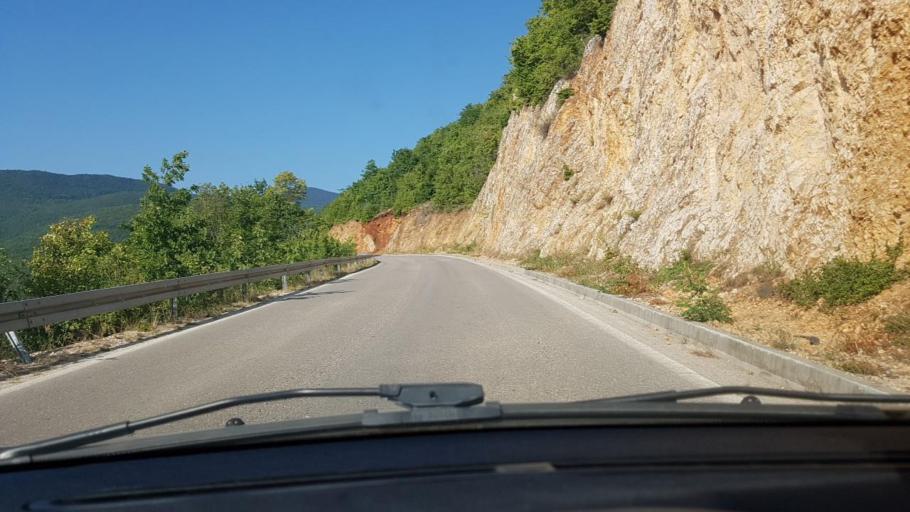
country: BA
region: Federation of Bosnia and Herzegovina
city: Rumboci
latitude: 43.8280
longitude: 17.4880
